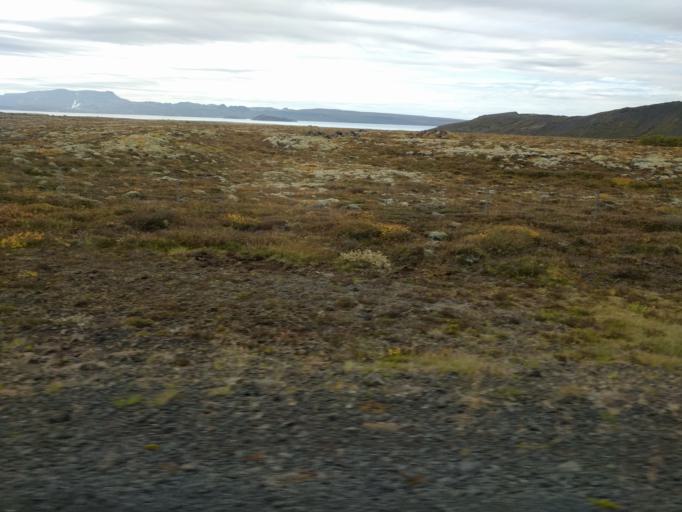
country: IS
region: South
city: Hveragerdi
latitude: 64.2133
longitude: -21.0477
